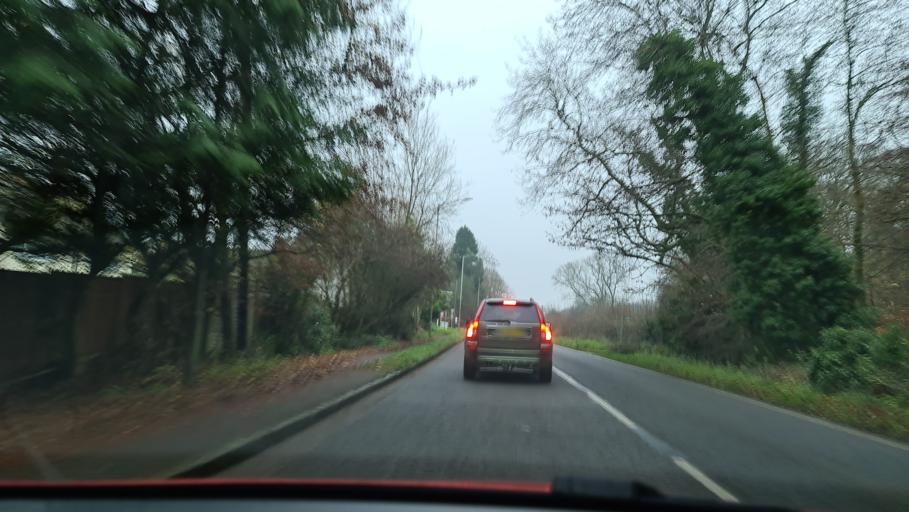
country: GB
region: England
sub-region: Buckinghamshire
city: Stokenchurch
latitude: 51.6505
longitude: -0.8632
